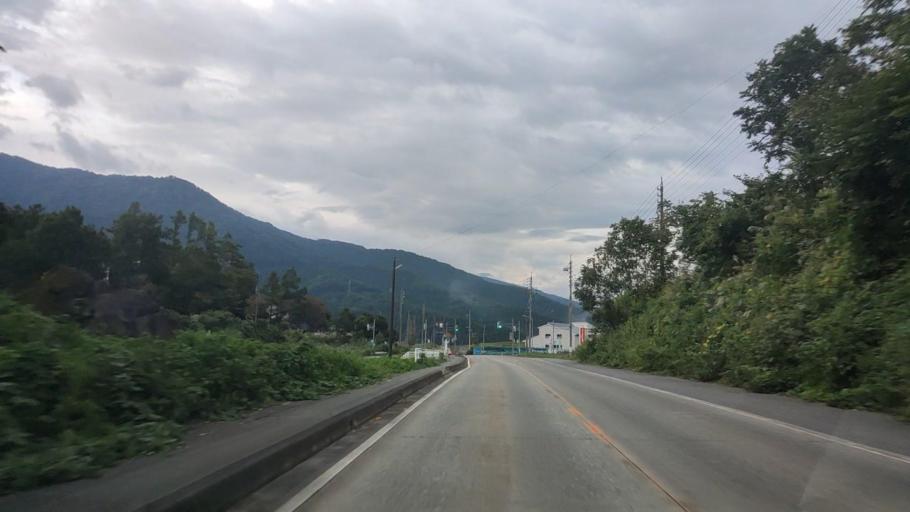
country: JP
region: Nagano
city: Iiyama
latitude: 36.8874
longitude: 138.4095
